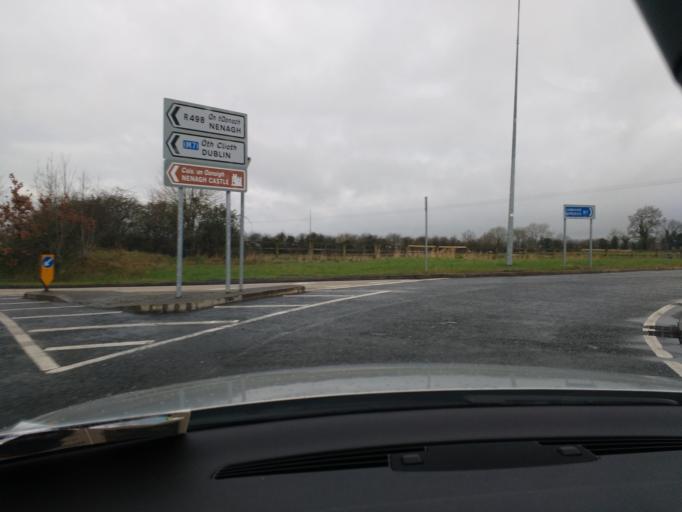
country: IE
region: Munster
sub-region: North Tipperary
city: Nenagh
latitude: 52.8478
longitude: -8.1565
